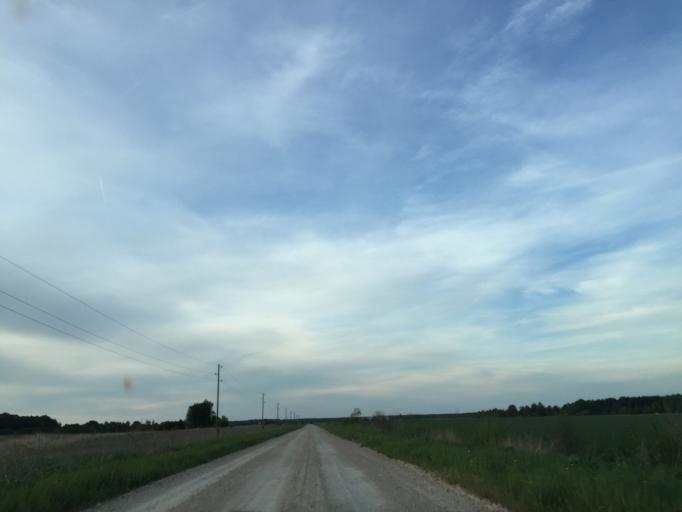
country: LV
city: Tireli
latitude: 56.7953
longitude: 23.5664
